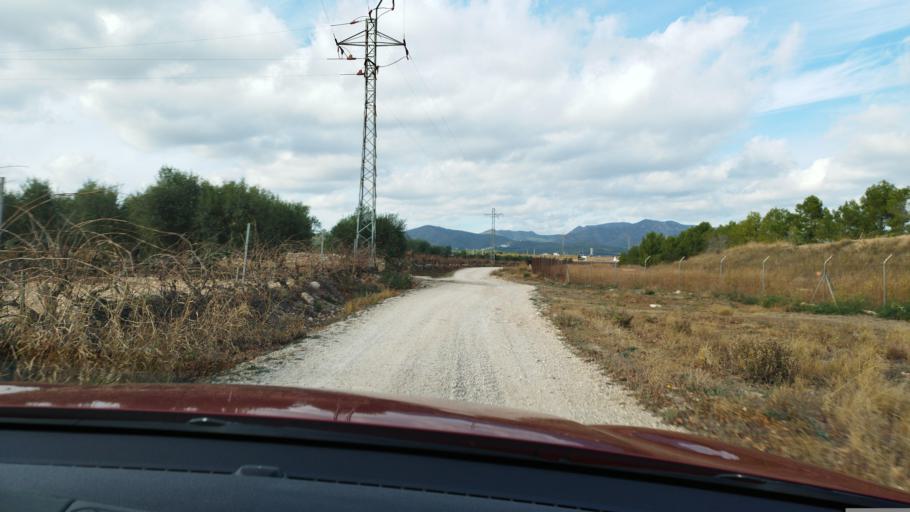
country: ES
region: Catalonia
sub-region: Provincia de Tarragona
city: Albinyana
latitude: 41.2613
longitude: 1.5010
